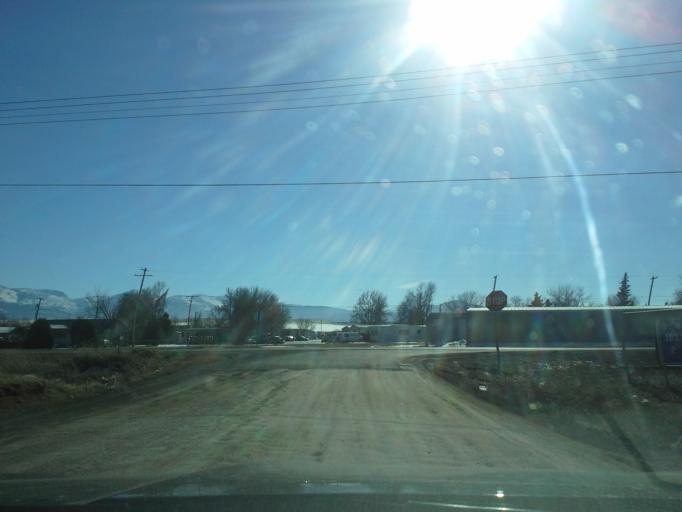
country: US
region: Montana
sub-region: Lewis and Clark County
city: East Helena
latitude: 46.5886
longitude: -111.8990
